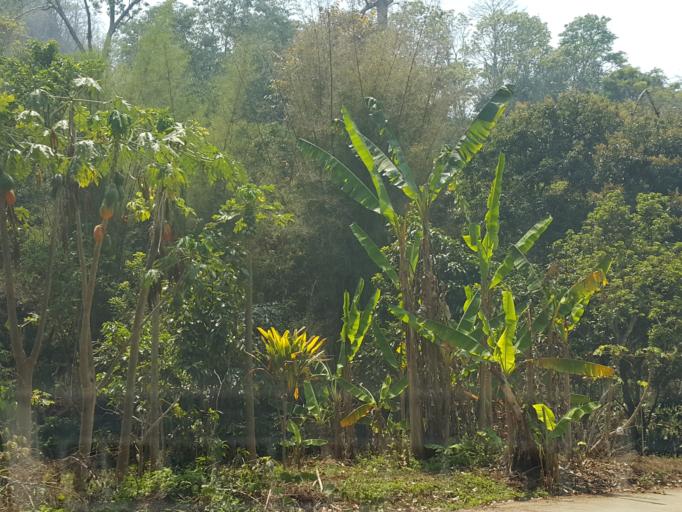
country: TH
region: Chiang Mai
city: Samoeng
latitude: 18.7992
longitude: 98.7954
